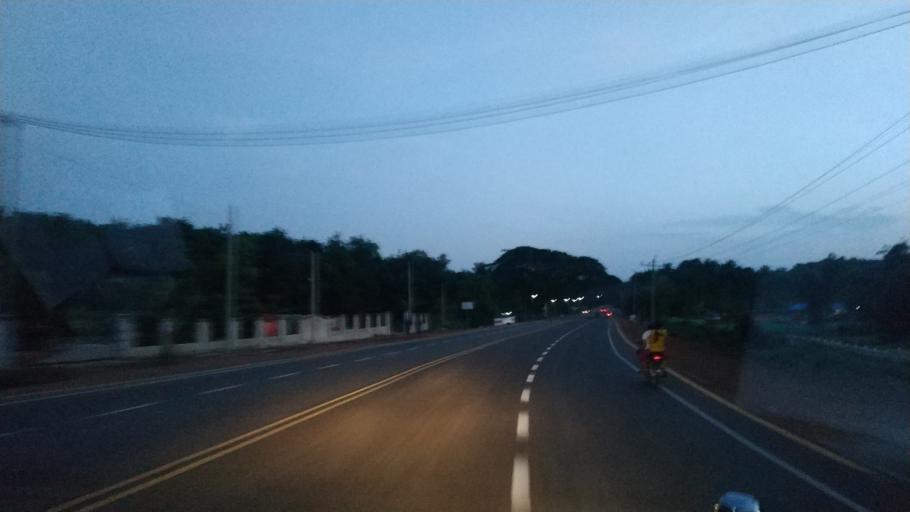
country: MM
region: Mon
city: Kyaikto
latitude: 17.3669
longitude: 97.0489
